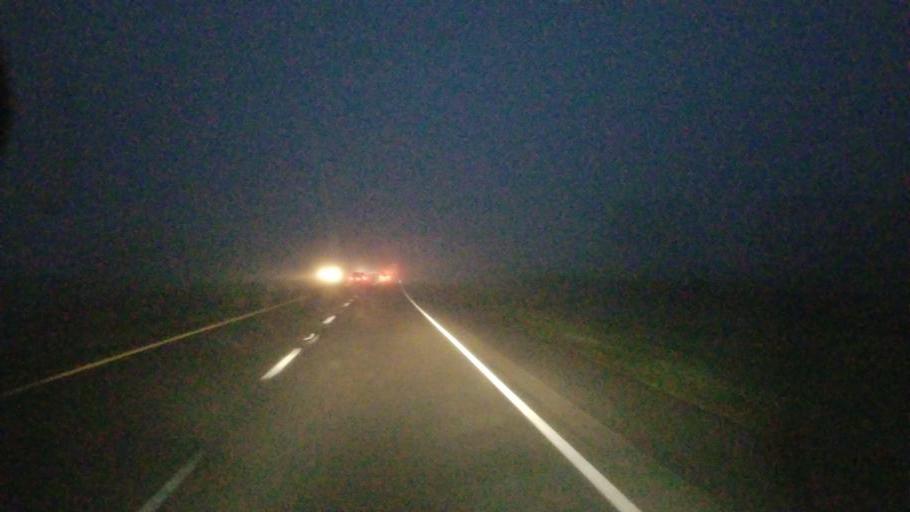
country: US
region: Ohio
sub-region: Ross County
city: Chillicothe
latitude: 39.3647
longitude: -82.9665
